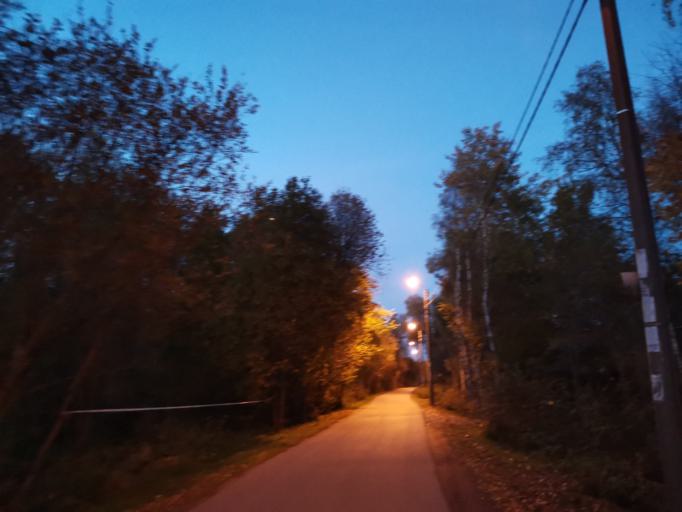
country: RU
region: St.-Petersburg
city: Beloostrov
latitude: 60.1397
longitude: 30.0051
